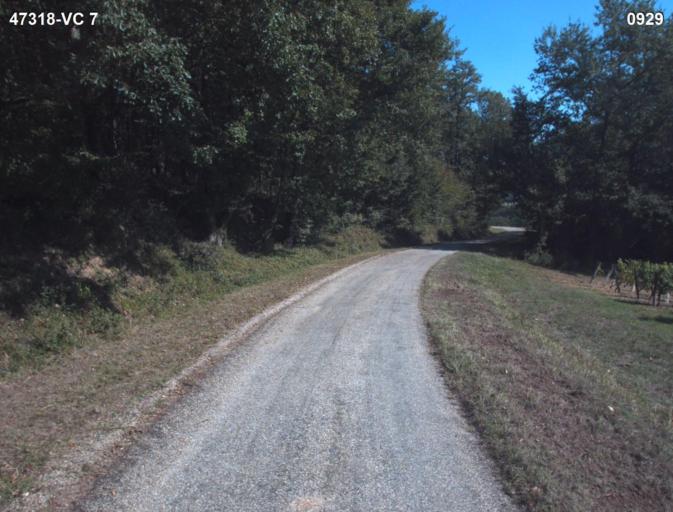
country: FR
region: Aquitaine
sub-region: Departement du Lot-et-Garonne
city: Buzet-sur-Baise
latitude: 44.2290
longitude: 0.3134
